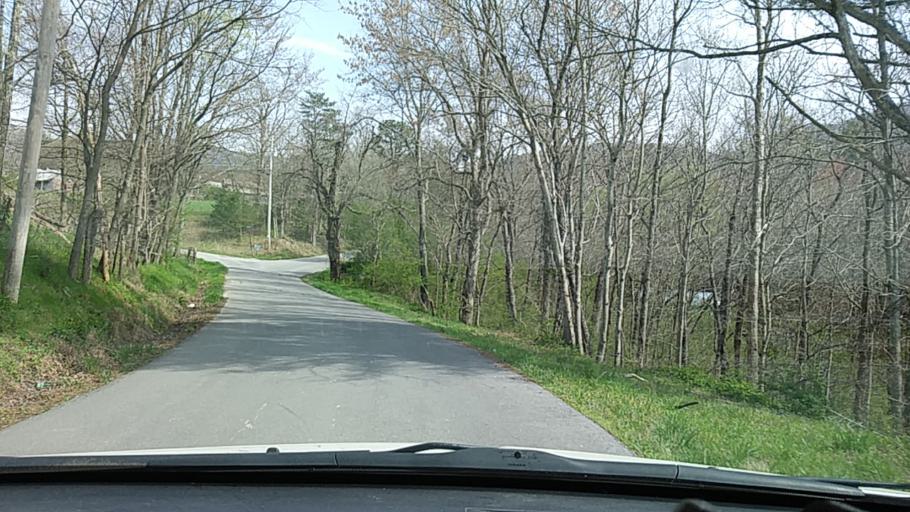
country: US
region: Tennessee
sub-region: Greene County
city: Tusculum
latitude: 36.0936
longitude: -82.7030
